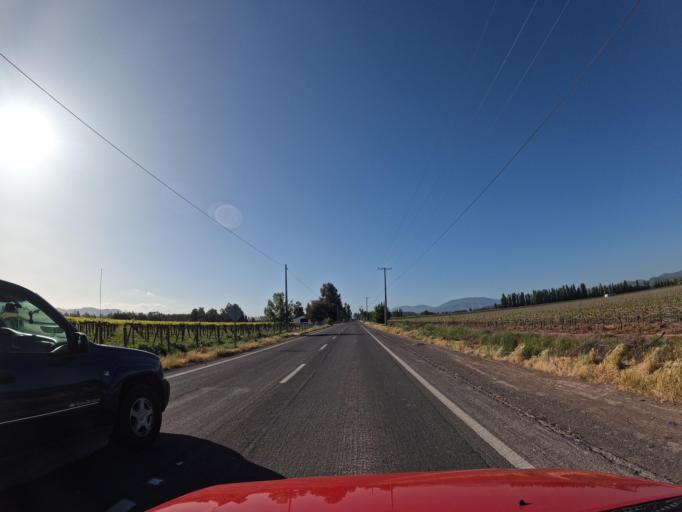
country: CL
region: Maule
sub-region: Provincia de Curico
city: Teno
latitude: -34.7641
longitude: -71.2375
